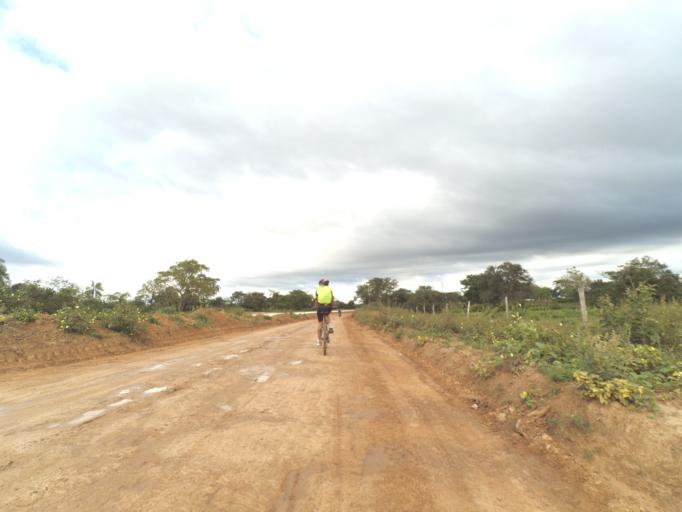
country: BO
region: Santa Cruz
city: Santa Cruz de la Sierra
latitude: -17.7127
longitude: -63.2743
